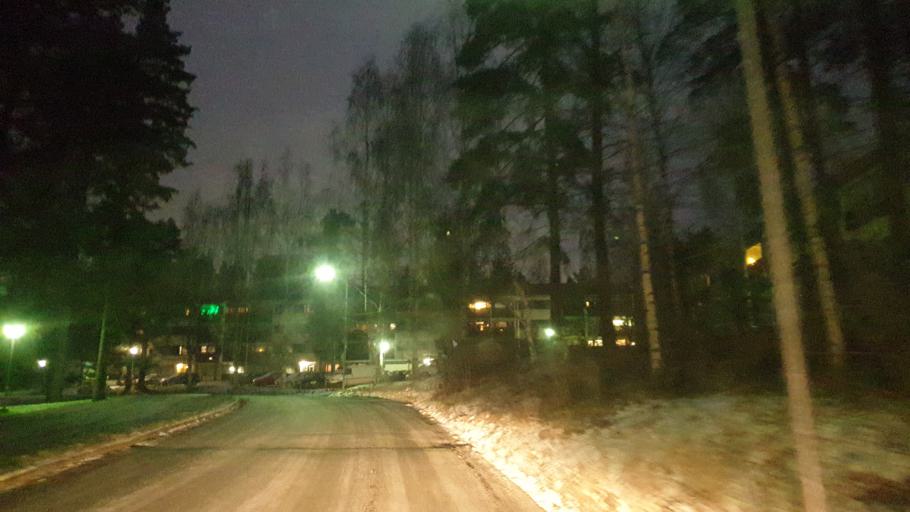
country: FI
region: Southern Savonia
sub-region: Savonlinna
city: Savonlinna
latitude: 61.8591
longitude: 28.9543
